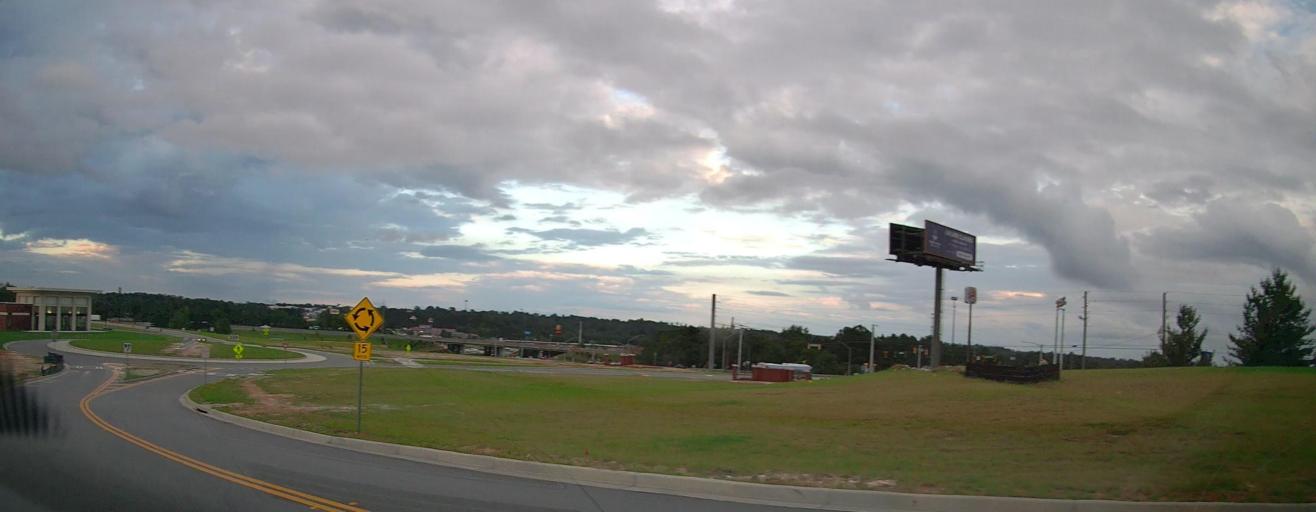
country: US
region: Georgia
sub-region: Bibb County
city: West Point
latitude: 32.8080
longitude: -83.7304
